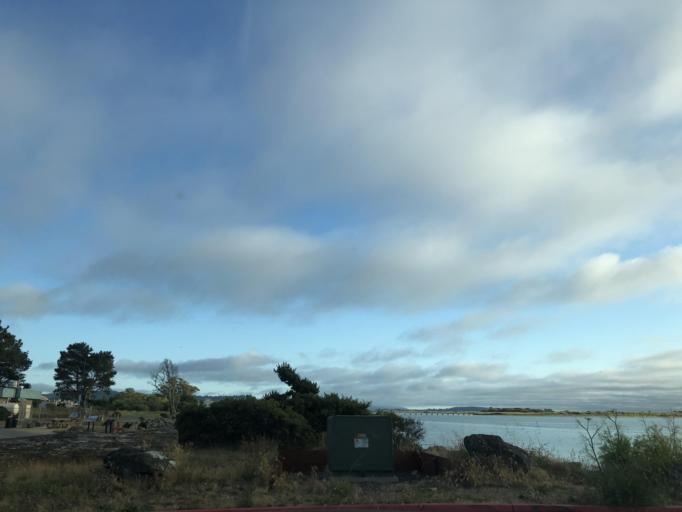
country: US
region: California
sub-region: Humboldt County
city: Bayview
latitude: 40.7768
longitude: -124.1936
